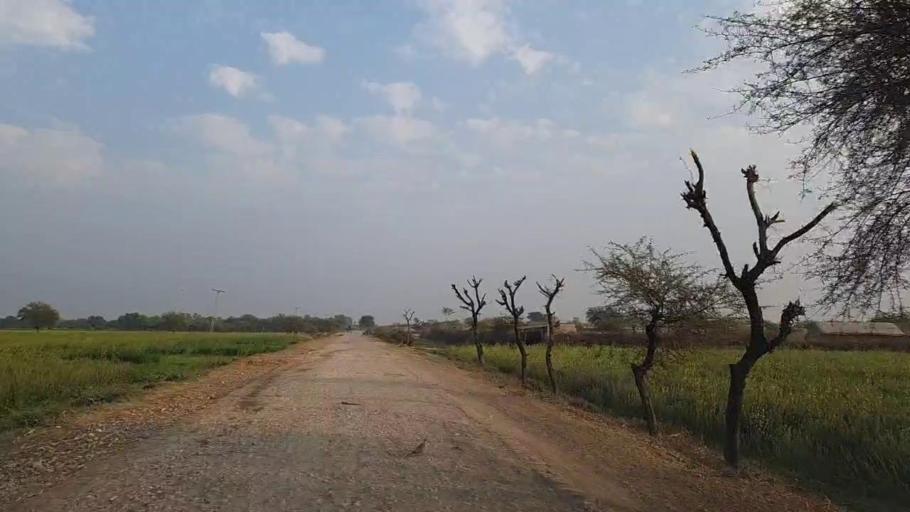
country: PK
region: Sindh
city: Samaro
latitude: 25.2929
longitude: 69.2303
